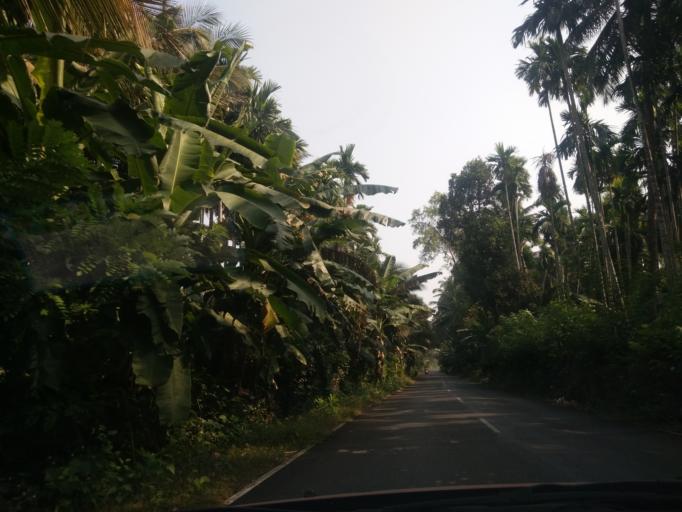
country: IN
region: Goa
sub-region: North Goa
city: Palle
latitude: 15.4768
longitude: 74.1206
